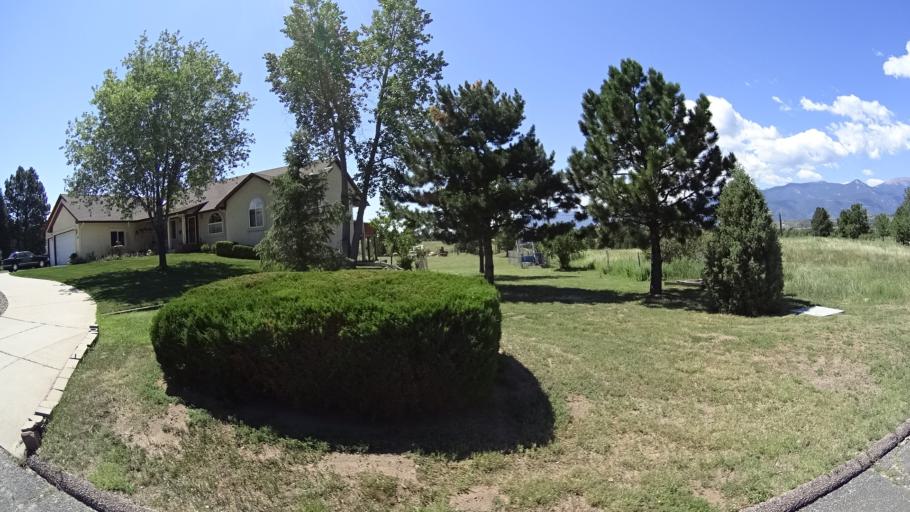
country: US
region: Colorado
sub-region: El Paso County
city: Colorado Springs
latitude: 38.9028
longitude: -104.8128
